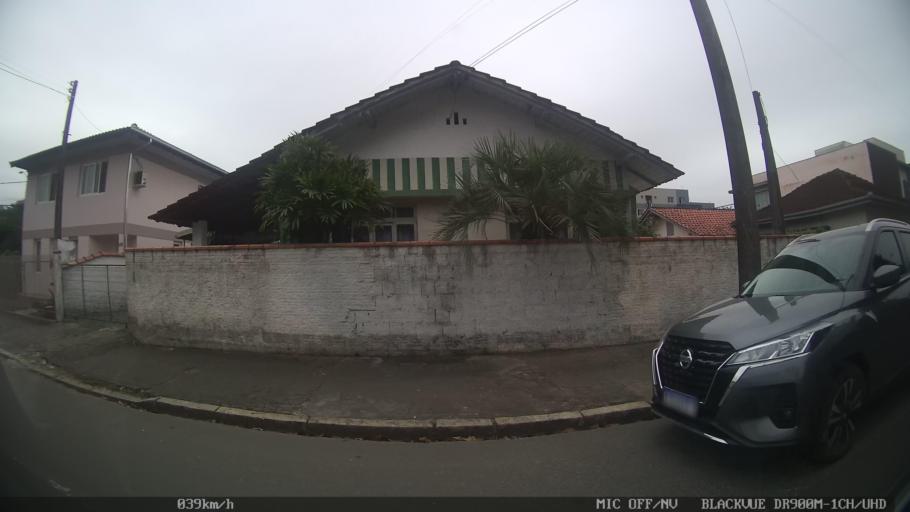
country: BR
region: Santa Catarina
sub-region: Joinville
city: Joinville
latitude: -26.2797
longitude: -48.8394
